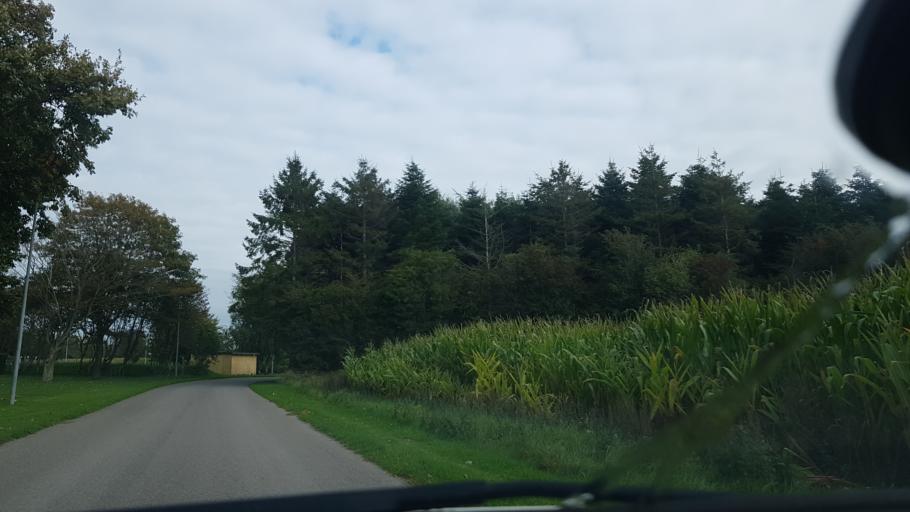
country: DK
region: South Denmark
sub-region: Vejen Kommune
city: Holsted
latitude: 55.4481
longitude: 8.9340
